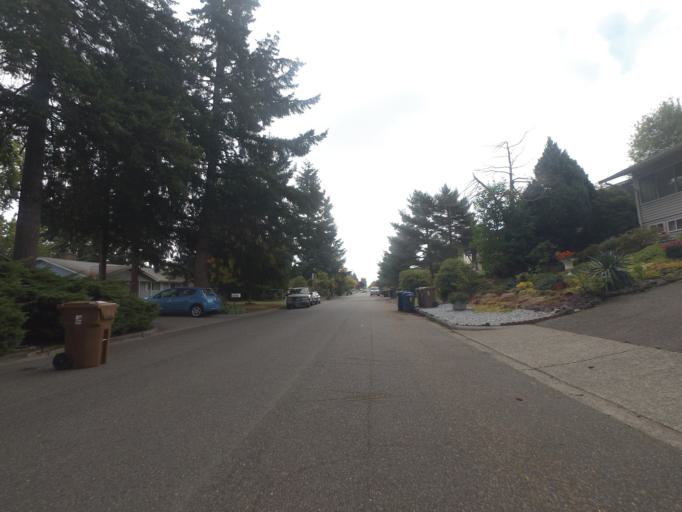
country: US
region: Washington
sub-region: Pierce County
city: Fircrest
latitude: 47.2059
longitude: -122.5021
